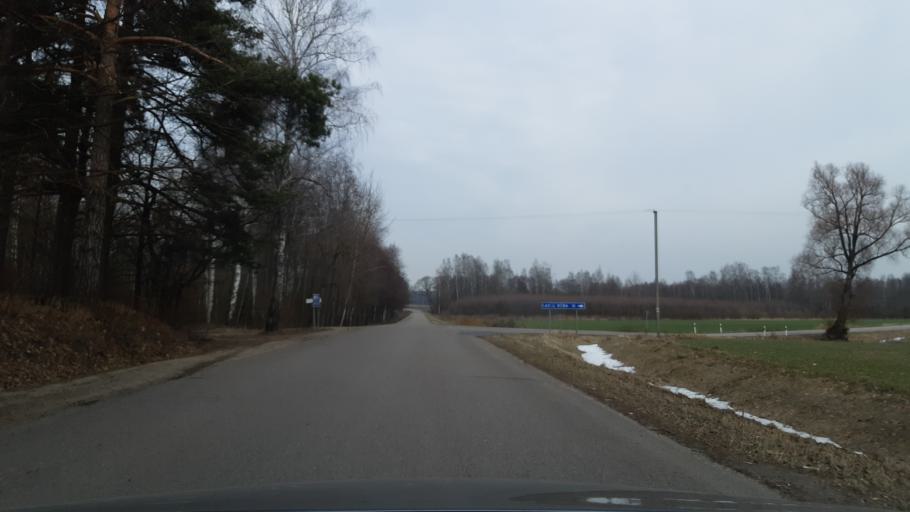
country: LT
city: Kazlu Ruda
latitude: 54.7324
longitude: 23.3402
